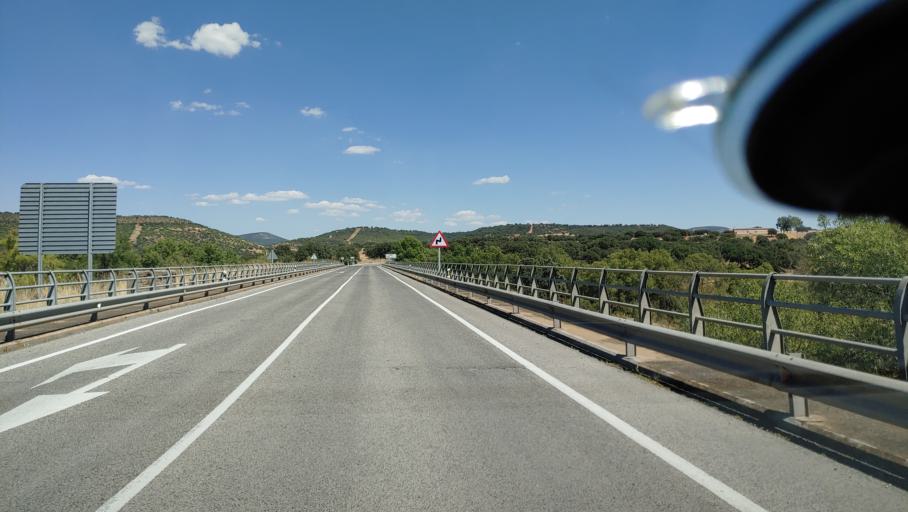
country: ES
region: Castille-La Mancha
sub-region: Provincia de Ciudad Real
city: Saceruela
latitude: 39.0170
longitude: -4.4927
